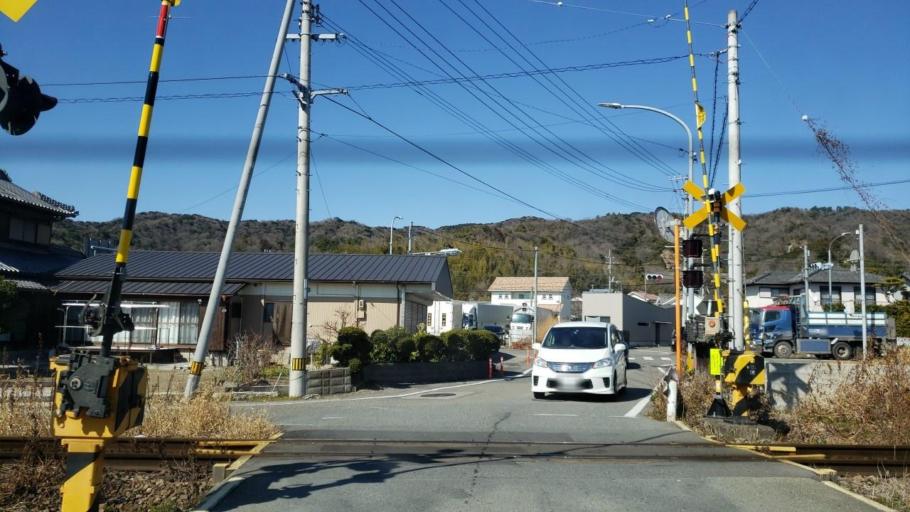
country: JP
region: Tokushima
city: Narutocho-mitsuishi
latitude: 34.1554
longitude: 134.5315
